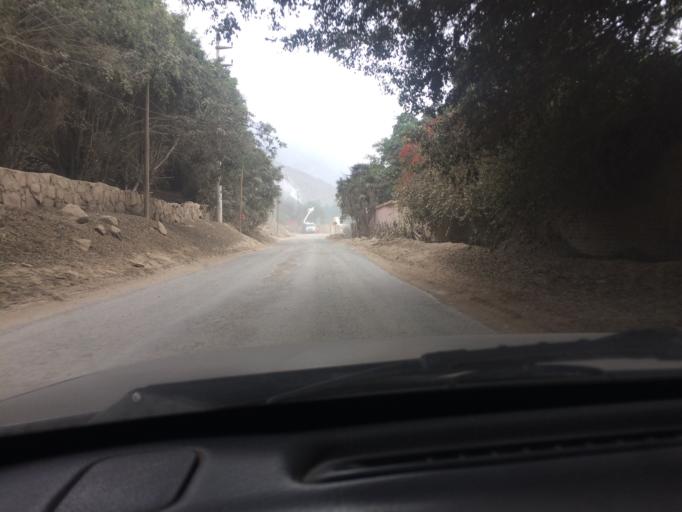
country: PE
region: Lima
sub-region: Lima
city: Cieneguilla
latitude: -12.1815
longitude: -76.8643
